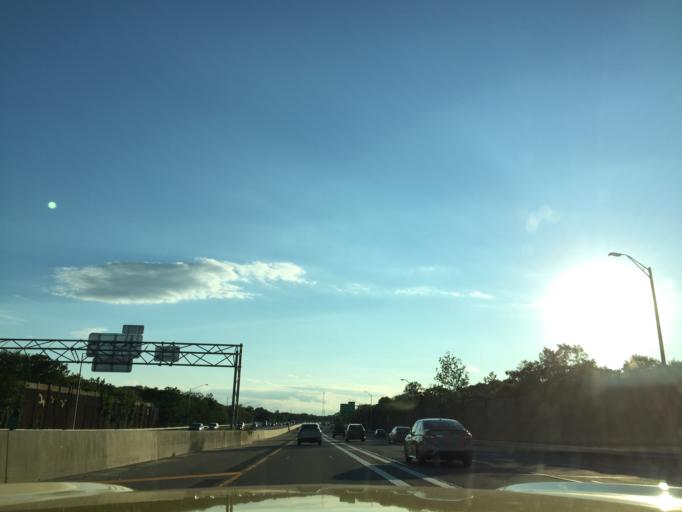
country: US
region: New York
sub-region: Suffolk County
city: Islandia
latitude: 40.8105
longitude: -73.1498
